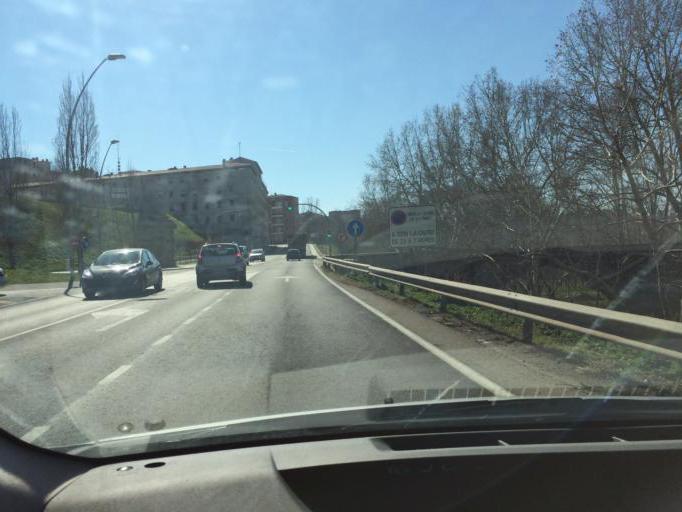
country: ES
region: Catalonia
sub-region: Provincia de Barcelona
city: Manresa
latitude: 41.7286
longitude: 1.8147
